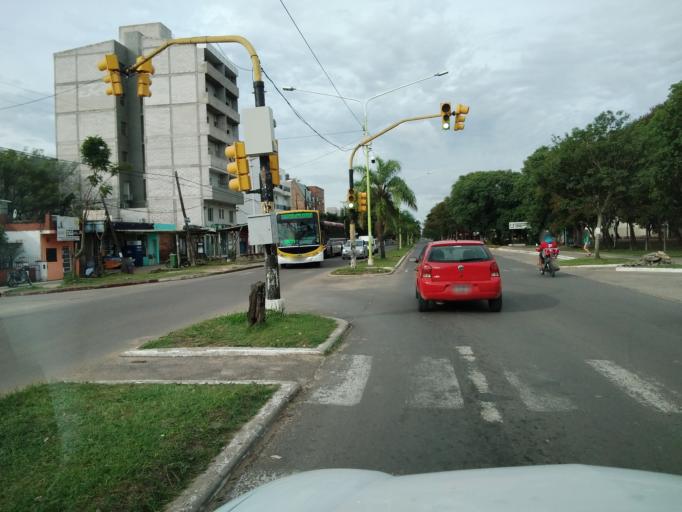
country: AR
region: Corrientes
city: Corrientes
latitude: -27.4653
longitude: -58.7841
